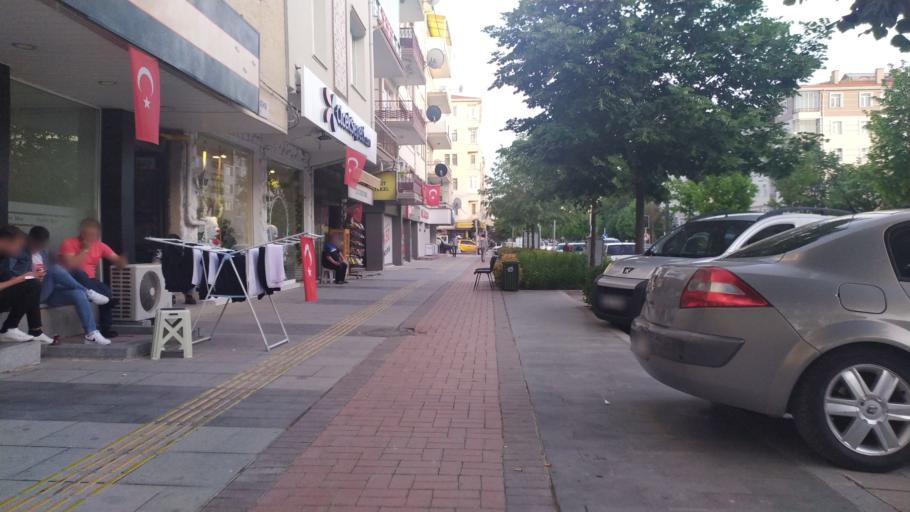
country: TR
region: Kirsehir
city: Kirsehir
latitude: 39.1525
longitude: 34.1597
